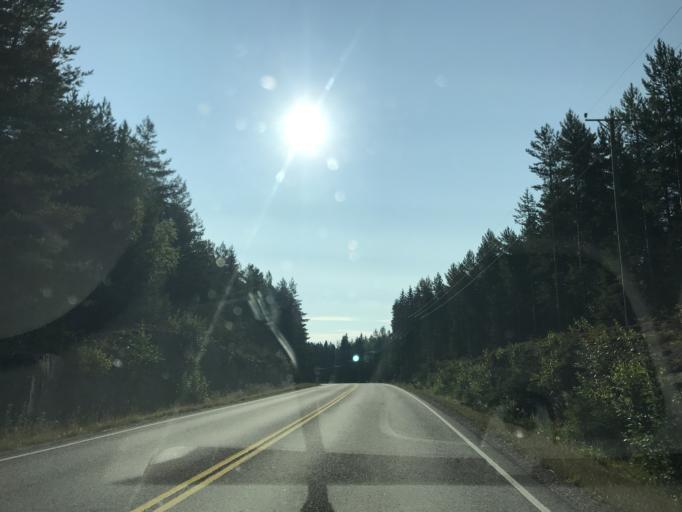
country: FI
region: Uusimaa
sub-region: Porvoo
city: Pukkila
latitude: 60.7684
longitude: 25.5060
